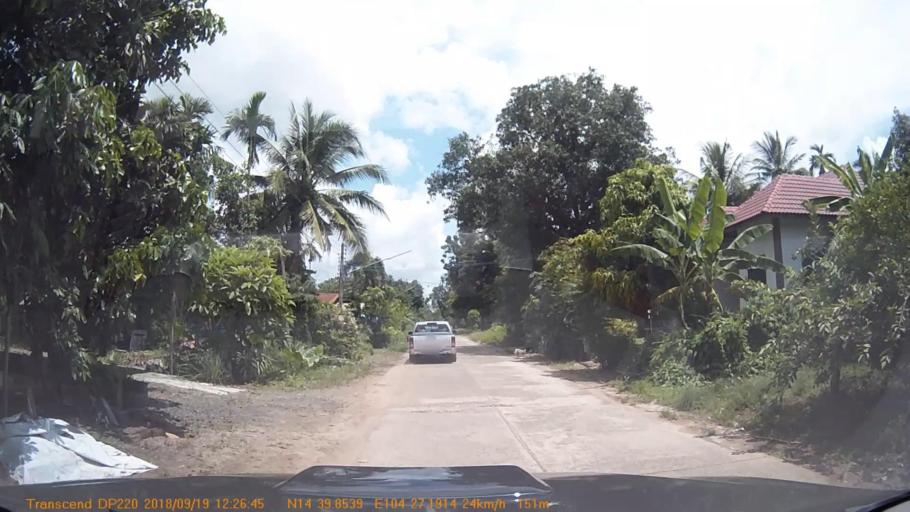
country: TH
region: Sisaket
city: Khun Han
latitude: 14.6642
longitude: 104.4533
